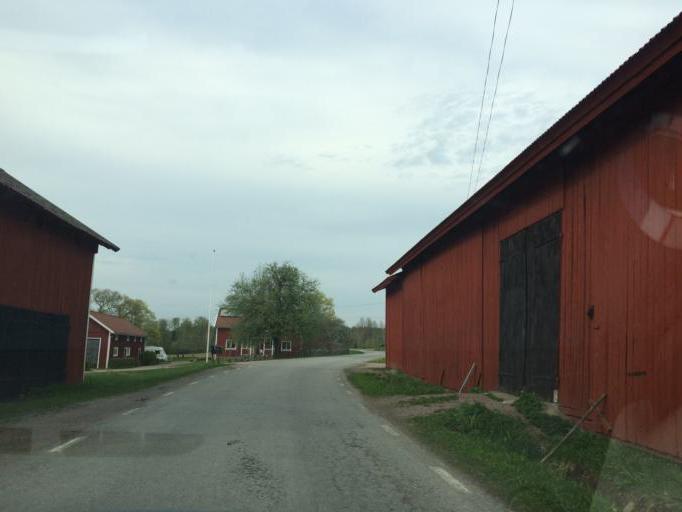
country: SE
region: Vaestmanland
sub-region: Kopings Kommun
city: Koping
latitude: 59.6129
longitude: 16.0310
